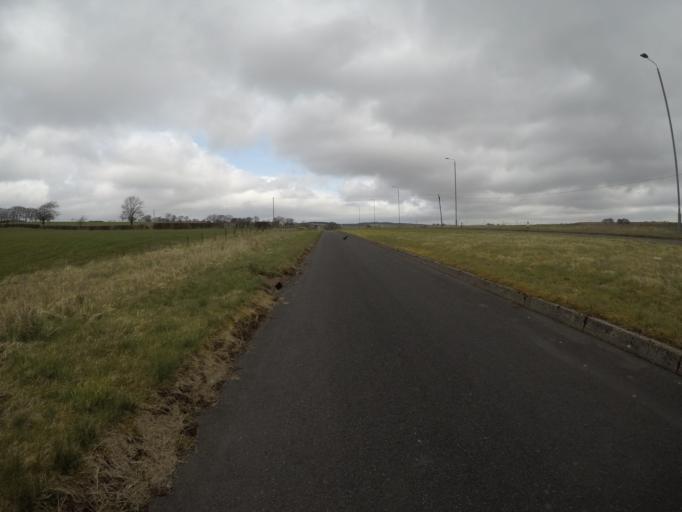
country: GB
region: Scotland
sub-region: East Ayrshire
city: Galston
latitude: 55.6823
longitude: -4.4214
